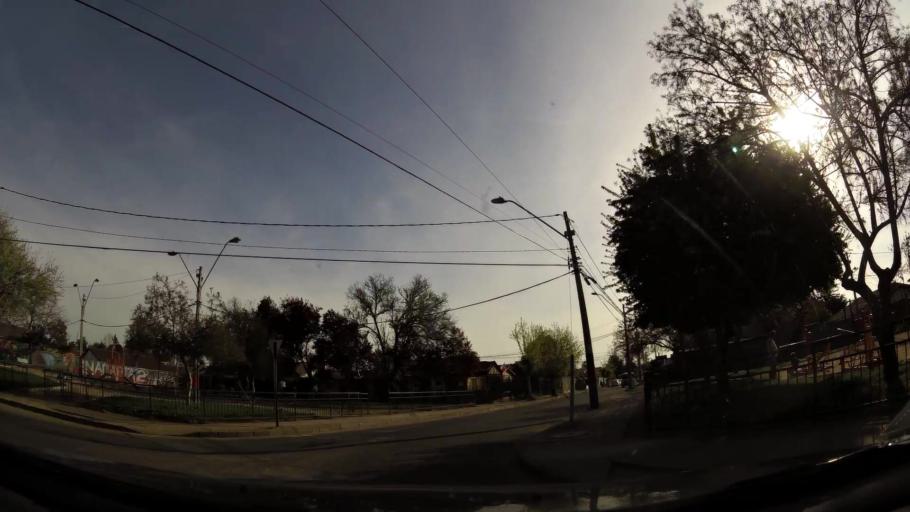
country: CL
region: Santiago Metropolitan
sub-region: Provincia de Cordillera
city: Puente Alto
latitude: -33.5777
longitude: -70.5617
